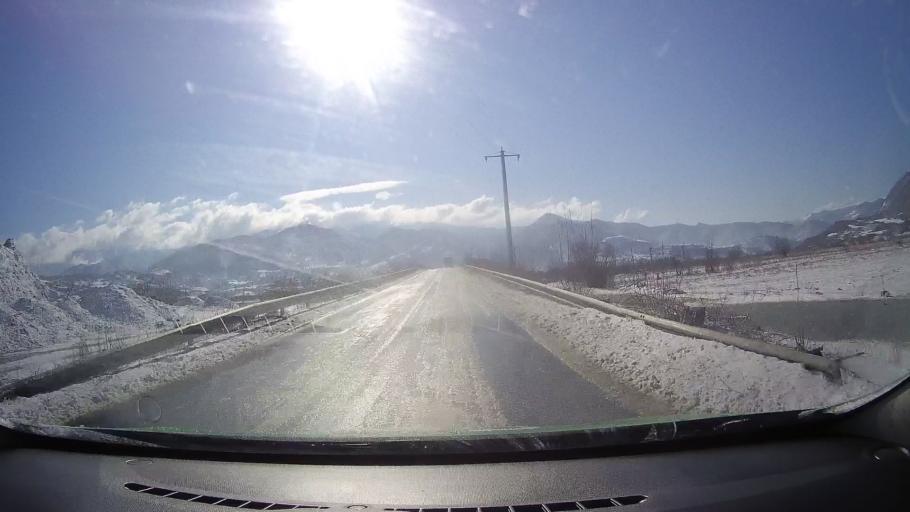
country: RO
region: Sibiu
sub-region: Comuna Turnu Rosu
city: Turnu Rosu
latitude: 45.6563
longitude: 24.2974
